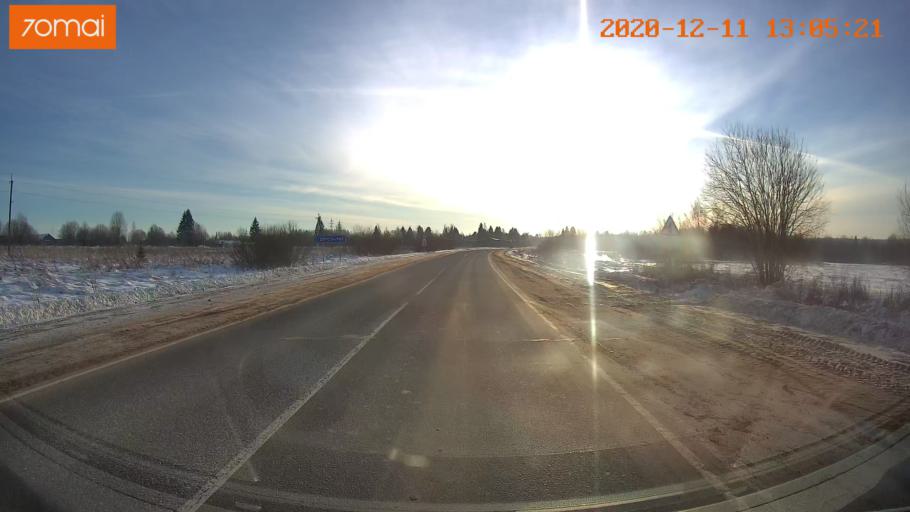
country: RU
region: Kostroma
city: Susanino
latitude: 58.2447
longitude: 41.6622
